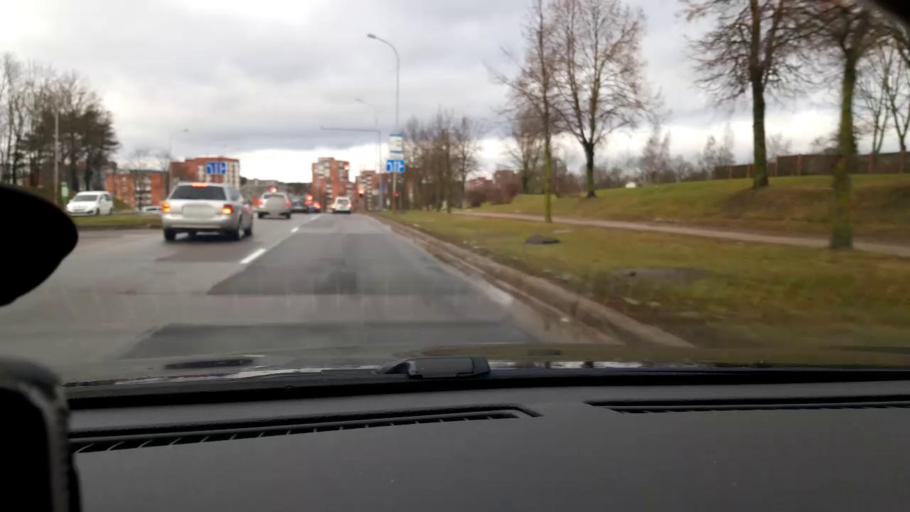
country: LT
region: Vilnius County
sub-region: Vilnius
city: Fabijoniskes
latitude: 54.7380
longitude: 25.2774
